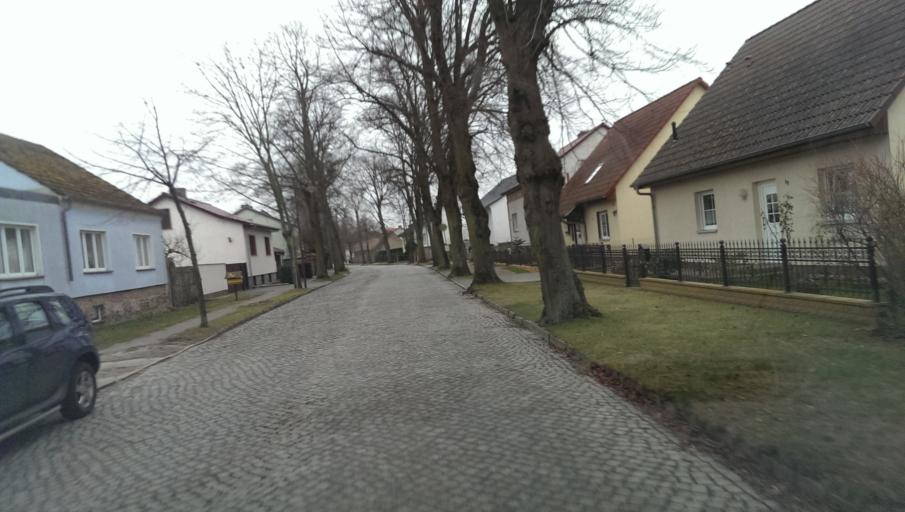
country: DE
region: Brandenburg
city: Mittenwalde
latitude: 52.2267
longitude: 13.5059
